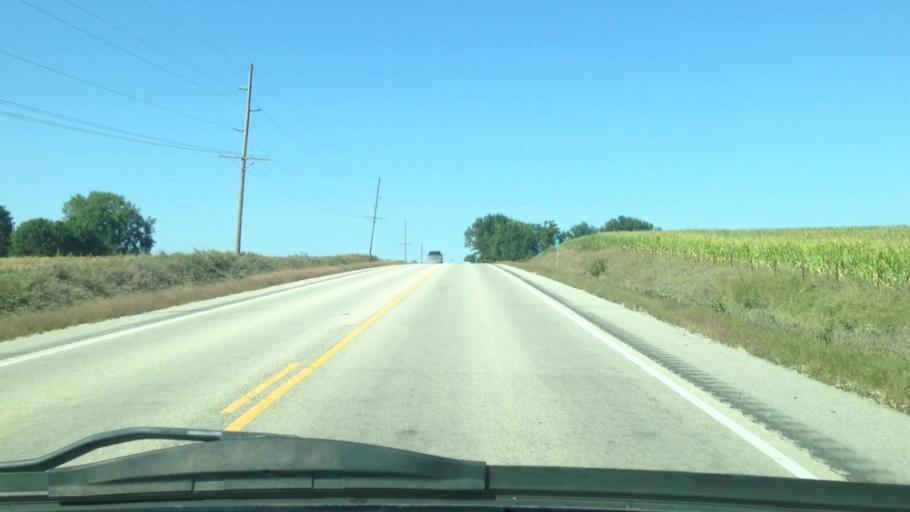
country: US
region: Minnesota
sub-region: Fillmore County
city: Rushford
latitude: 43.9056
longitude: -91.7401
